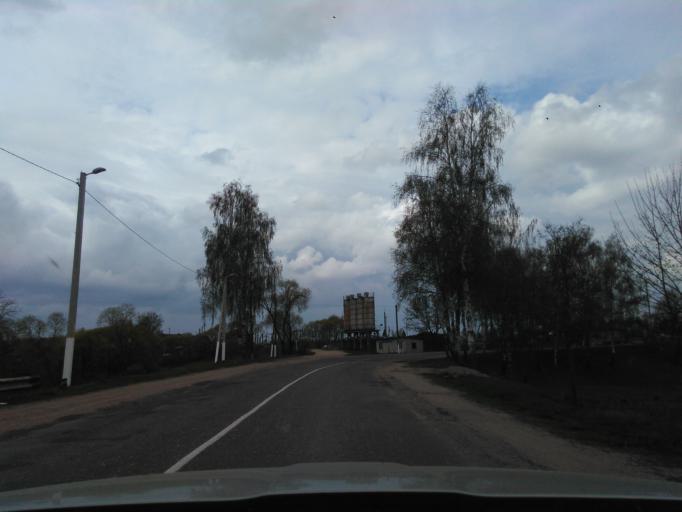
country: BY
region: Vitebsk
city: Chashniki
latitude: 54.8404
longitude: 29.1799
